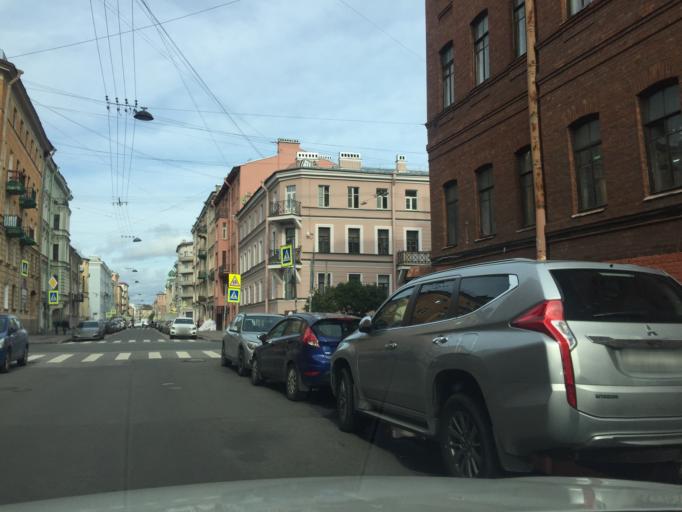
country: RU
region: St.-Petersburg
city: Centralniy
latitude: 59.9321
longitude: 30.3713
